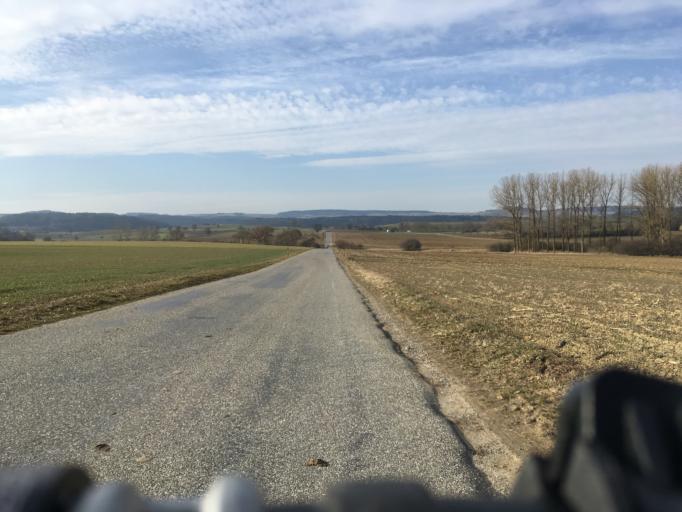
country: CH
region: Schaffhausen
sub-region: Bezirk Reiat
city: Thayngen
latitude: 47.7806
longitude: 8.7093
